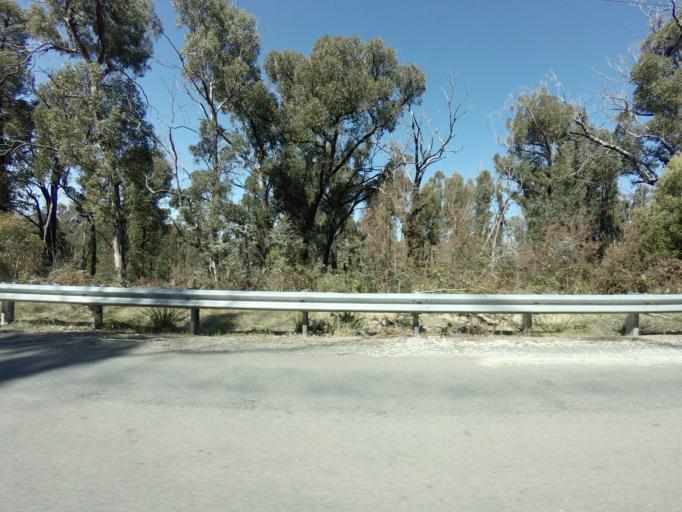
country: AU
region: Tasmania
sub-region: Derwent Valley
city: New Norfolk
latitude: -42.5515
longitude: 146.7138
